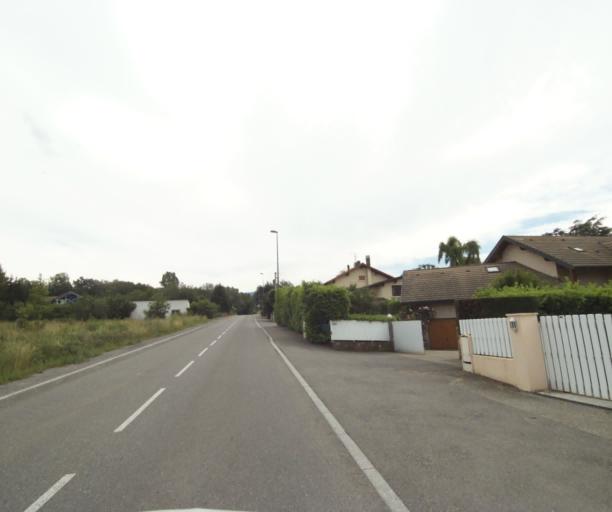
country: FR
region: Rhone-Alpes
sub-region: Departement de la Haute-Savoie
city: Sciez
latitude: 46.3271
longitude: 6.3927
